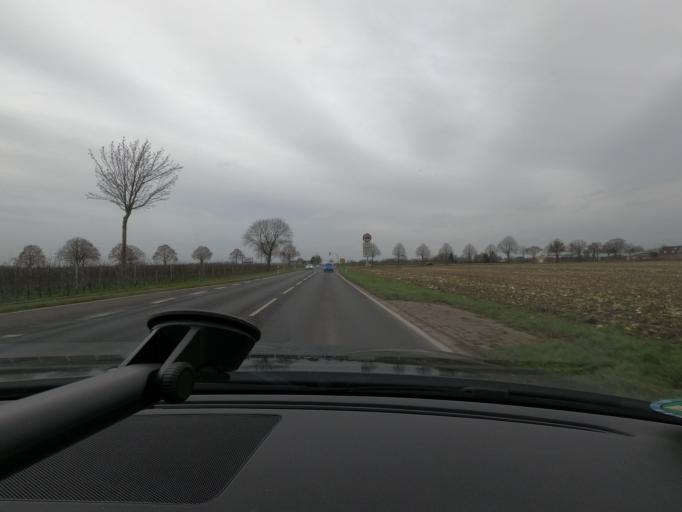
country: DE
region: North Rhine-Westphalia
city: Tonisvorst
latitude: 51.3372
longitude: 6.4978
